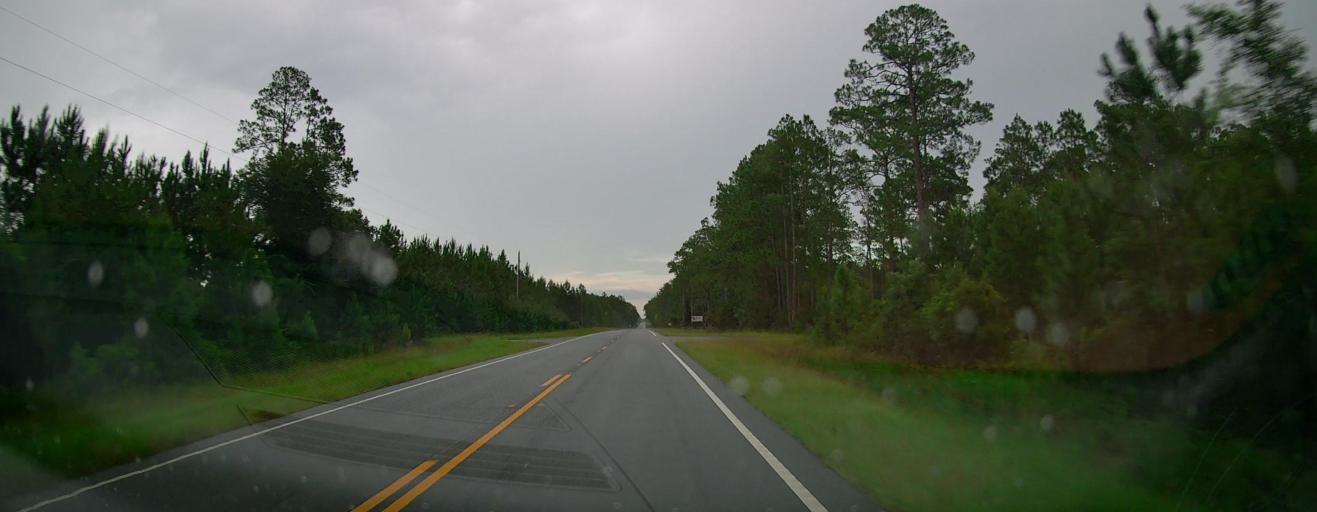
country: US
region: Georgia
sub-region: Brantley County
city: Nahunta
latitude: 31.3401
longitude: -81.8414
